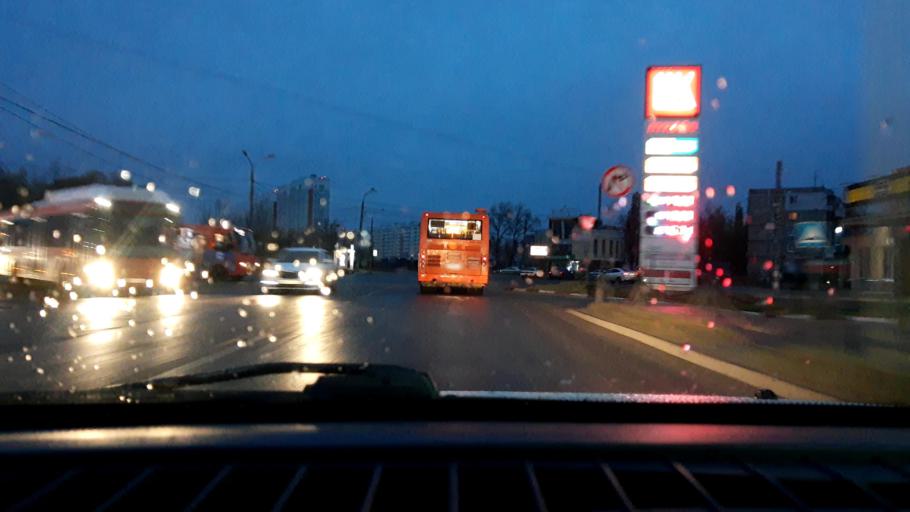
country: RU
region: Nizjnij Novgorod
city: Gorbatovka
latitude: 56.3576
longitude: 43.8057
